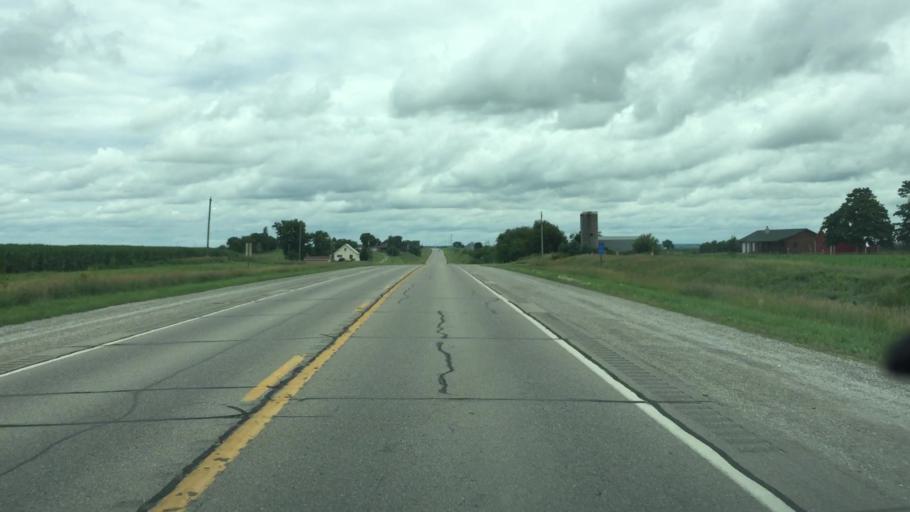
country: US
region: Iowa
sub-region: Jasper County
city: Monroe
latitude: 41.5578
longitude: -93.0971
